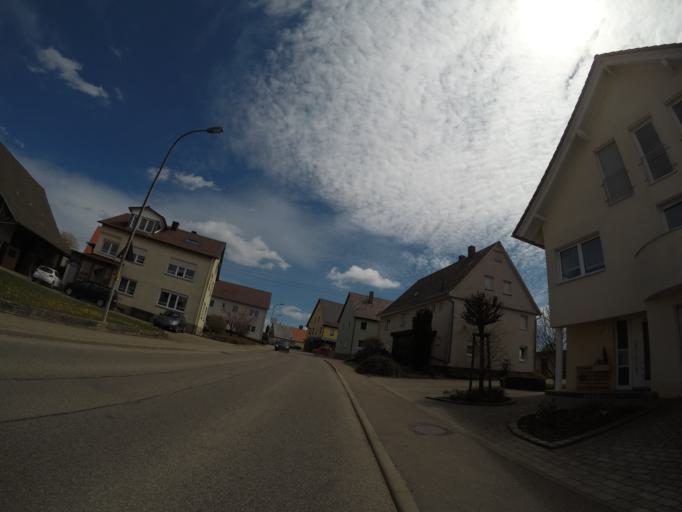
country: DE
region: Baden-Wuerttemberg
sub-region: Tuebingen Region
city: Westerheim
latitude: 48.5141
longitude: 9.6256
